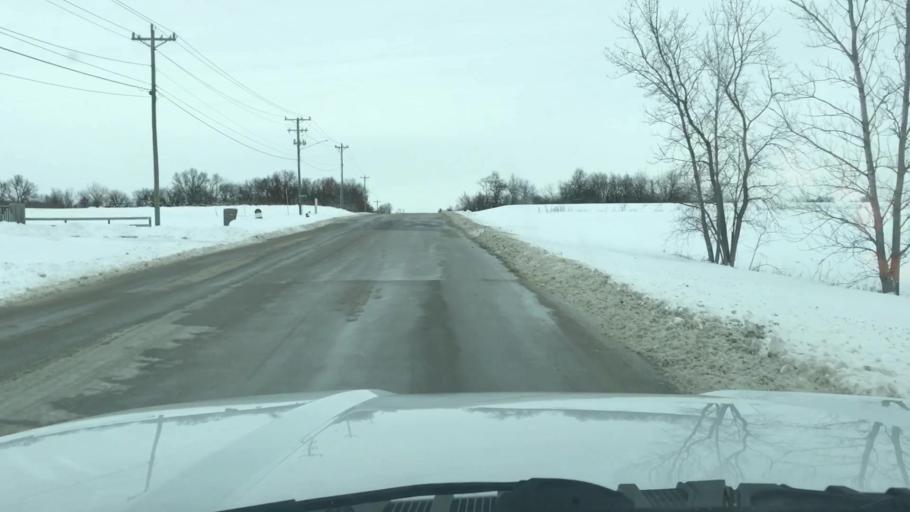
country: US
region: Missouri
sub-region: Clinton County
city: Cameron
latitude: 39.7438
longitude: -94.2153
